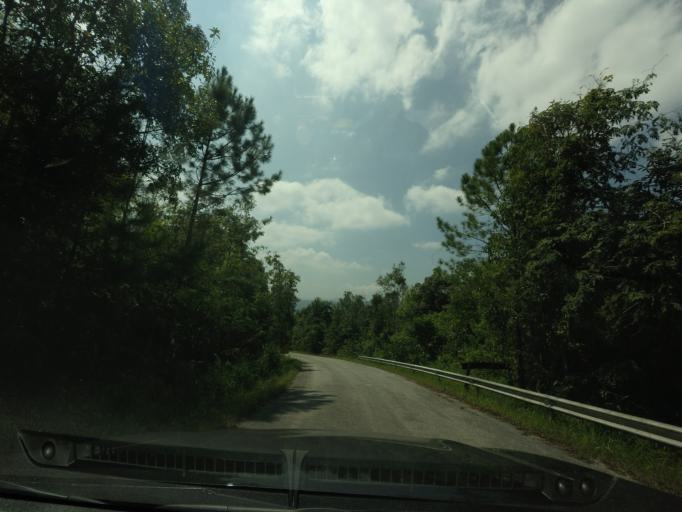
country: TH
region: Loei
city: Na Haeo
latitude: 17.4911
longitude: 100.9390
